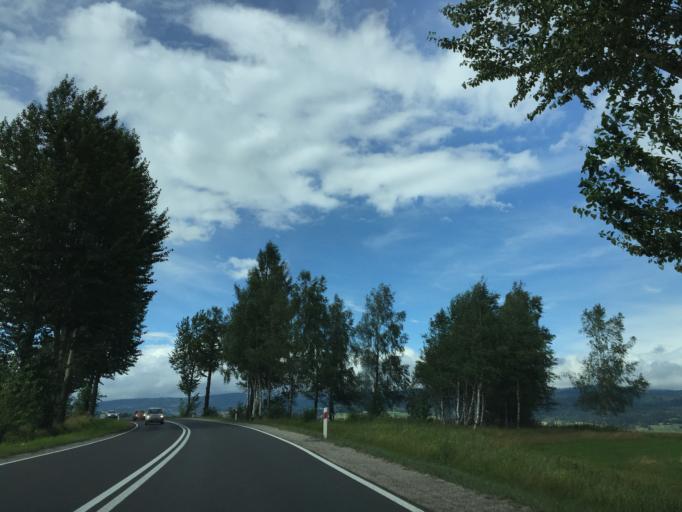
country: PL
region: Lesser Poland Voivodeship
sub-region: Powiat nowotarski
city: Waksmund
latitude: 49.4564
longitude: 20.0703
